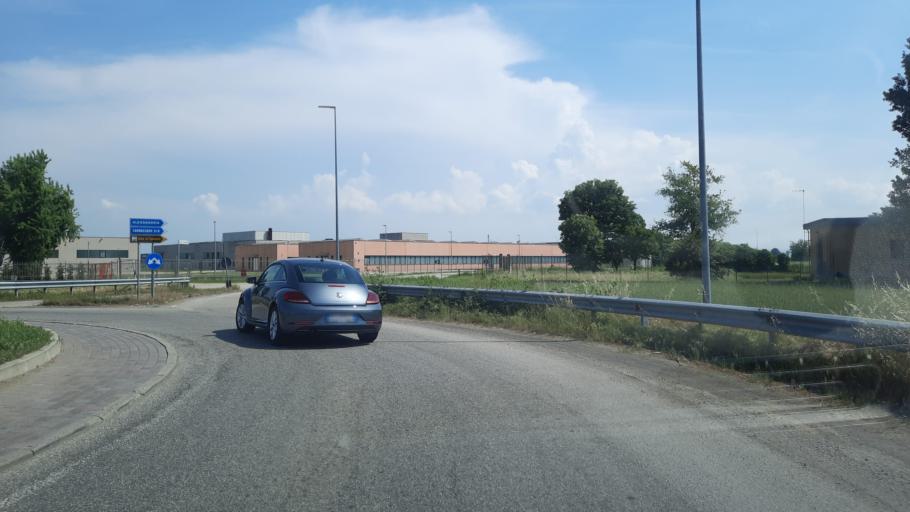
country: IT
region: Lombardy
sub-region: Provincia di Pavia
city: Carbonara al Ticino
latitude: 45.1623
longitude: 9.0651
